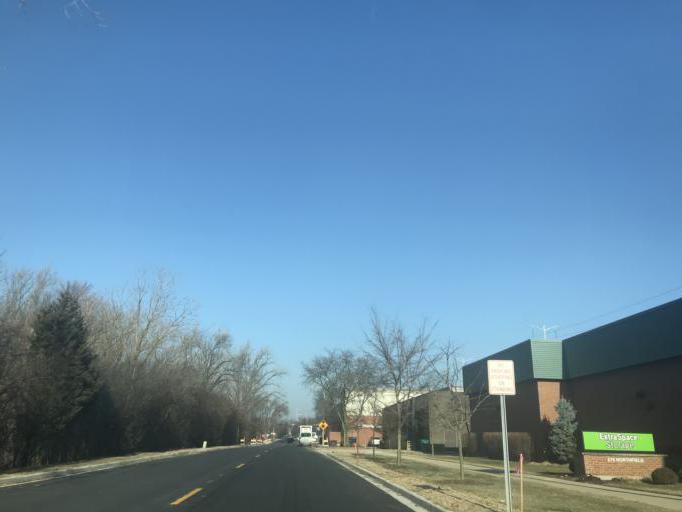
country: US
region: Illinois
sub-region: Cook County
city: Northfield
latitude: 42.0987
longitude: -87.7716
